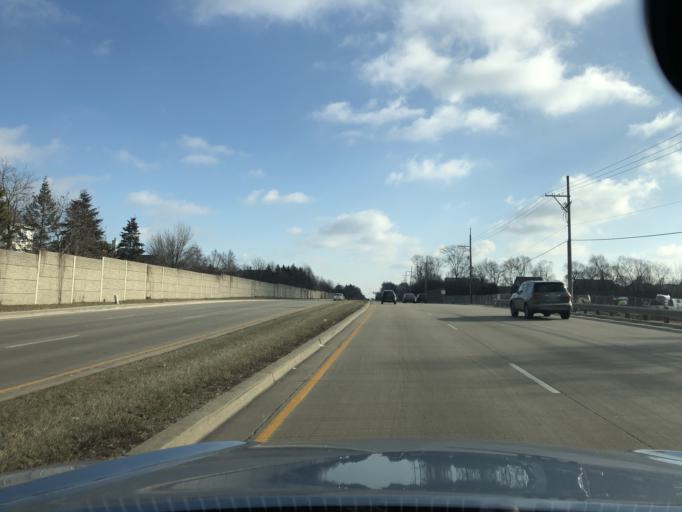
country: US
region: Illinois
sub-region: Cook County
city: Northbrook
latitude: 42.1058
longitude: -87.8643
